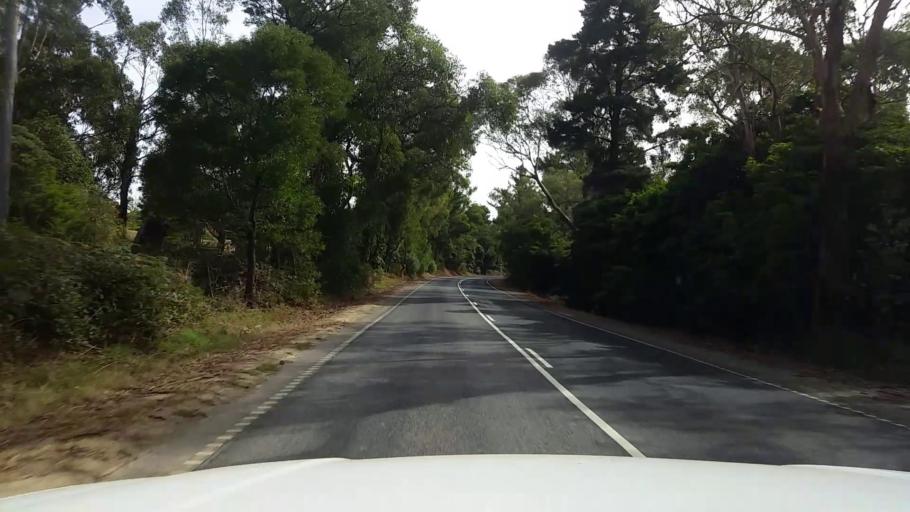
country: AU
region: Victoria
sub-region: Mornington Peninsula
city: Mount Martha
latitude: -38.2941
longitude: 145.0762
